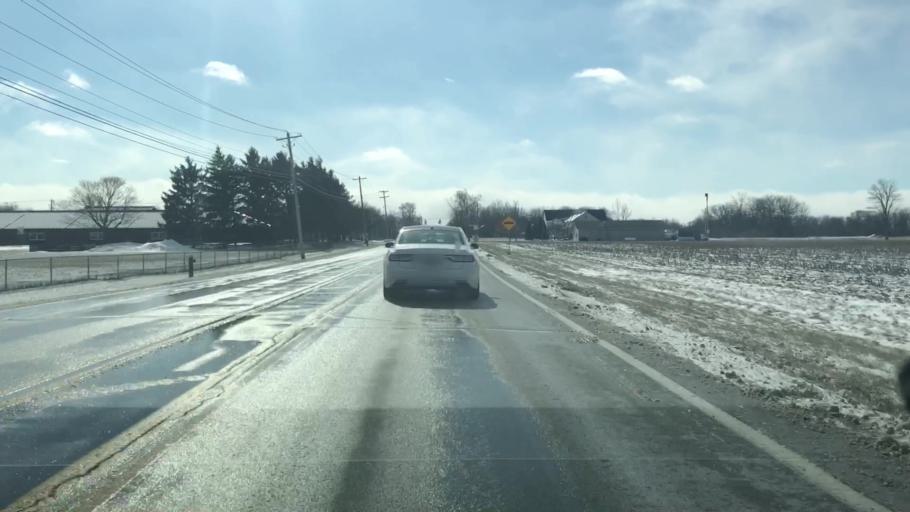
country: US
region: Ohio
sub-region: Franklin County
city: Lake Darby
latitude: 40.0020
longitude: -83.2021
